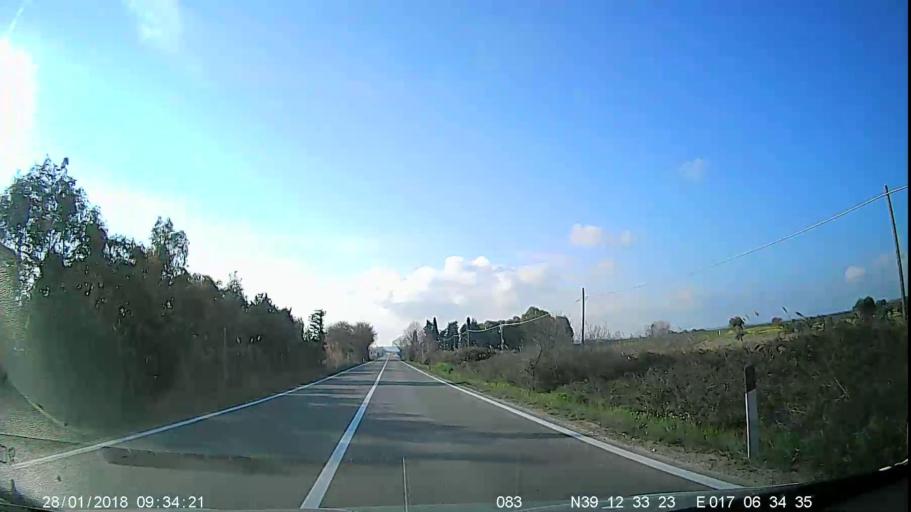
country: IT
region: Calabria
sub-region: Provincia di Crotone
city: Tronca
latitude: 39.2086
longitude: 17.1093
